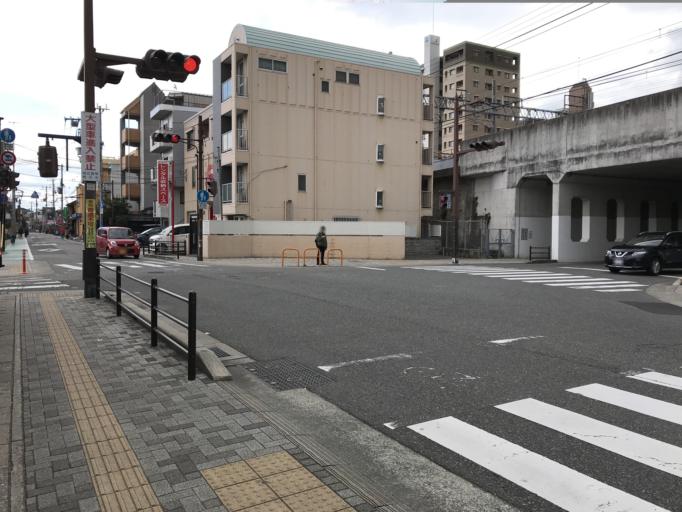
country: JP
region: Hyogo
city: Akashi
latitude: 34.6489
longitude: 134.9958
